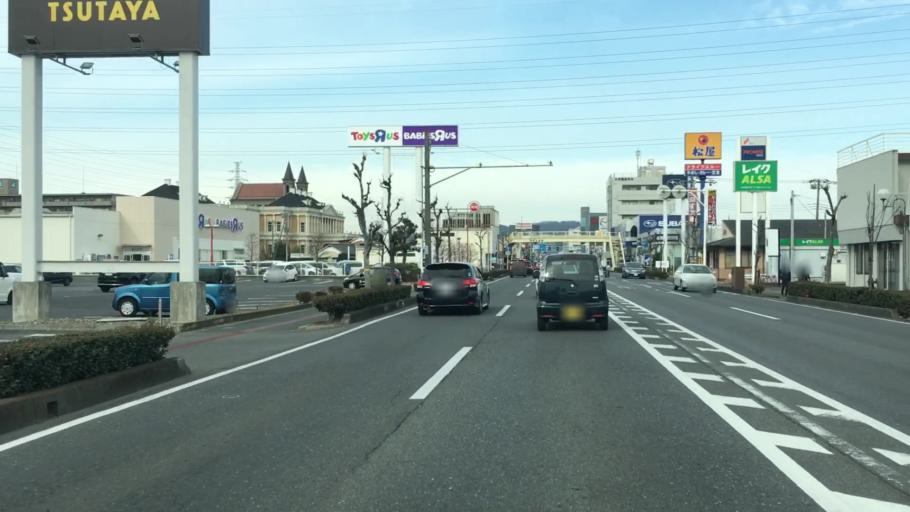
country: JP
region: Gunma
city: Ota
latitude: 36.2818
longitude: 139.3771
